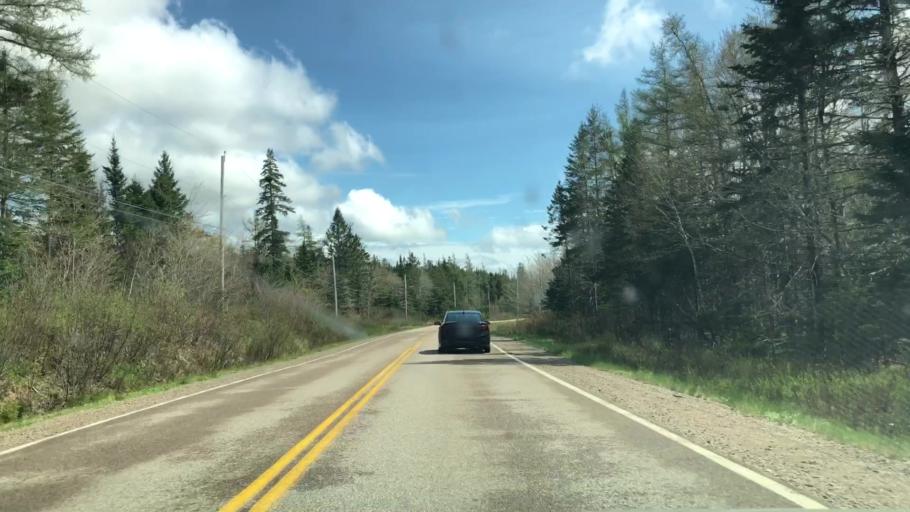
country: CA
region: Nova Scotia
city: Antigonish
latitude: 45.2109
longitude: -62.0044
